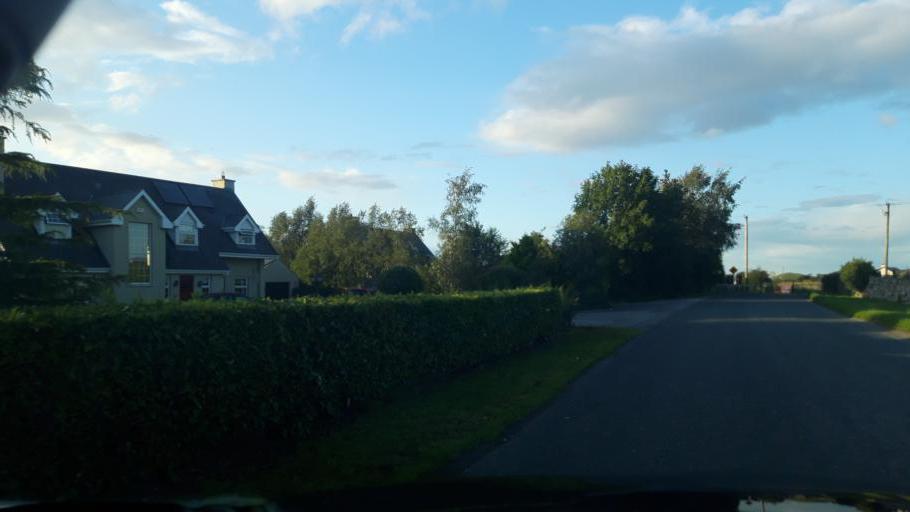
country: IE
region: Leinster
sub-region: An Iarmhi
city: Athlone
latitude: 53.4278
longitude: -7.8776
